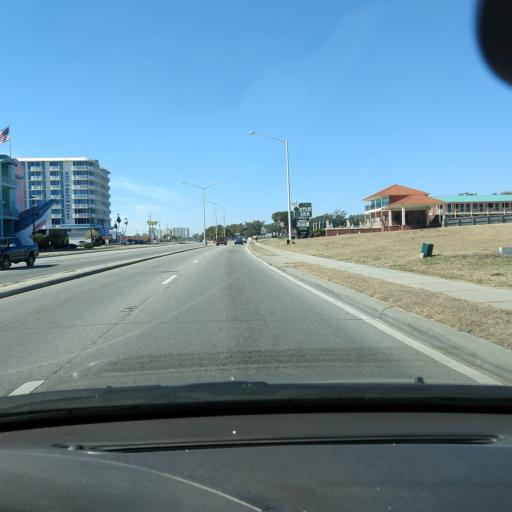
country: US
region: Mississippi
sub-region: Harrison County
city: Biloxi
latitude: 30.3937
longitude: -88.9388
